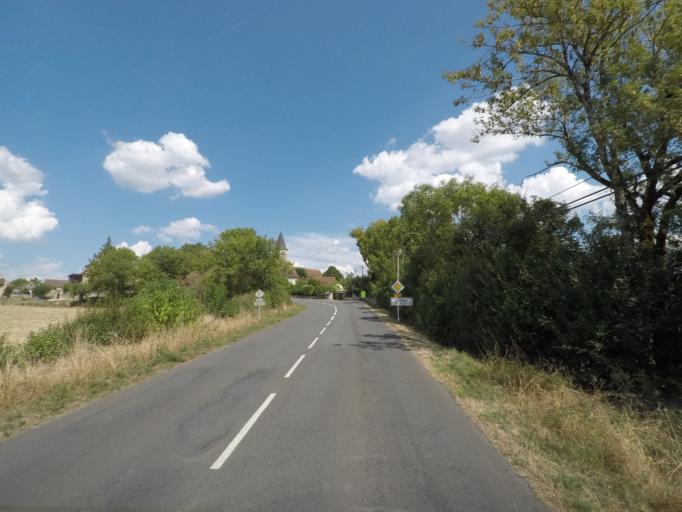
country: FR
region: Midi-Pyrenees
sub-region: Departement du Lot
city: Le Vigan
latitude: 44.6557
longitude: 1.5831
